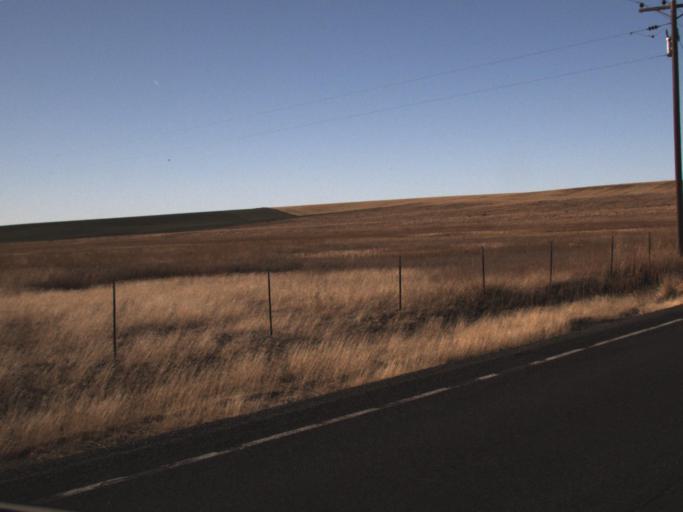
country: US
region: Washington
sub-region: Adams County
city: Ritzville
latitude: 47.0503
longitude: -118.3562
